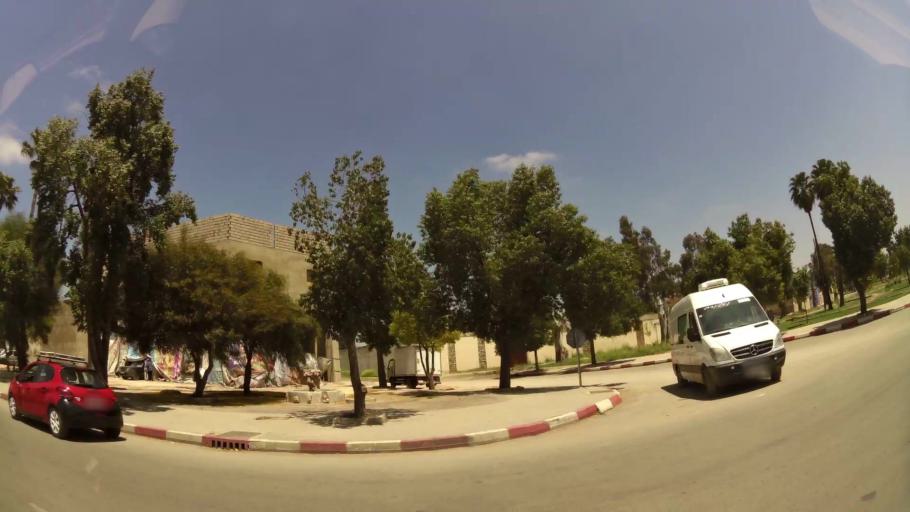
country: MA
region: Fes-Boulemane
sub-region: Fes
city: Fes
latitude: 34.0406
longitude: -5.0347
